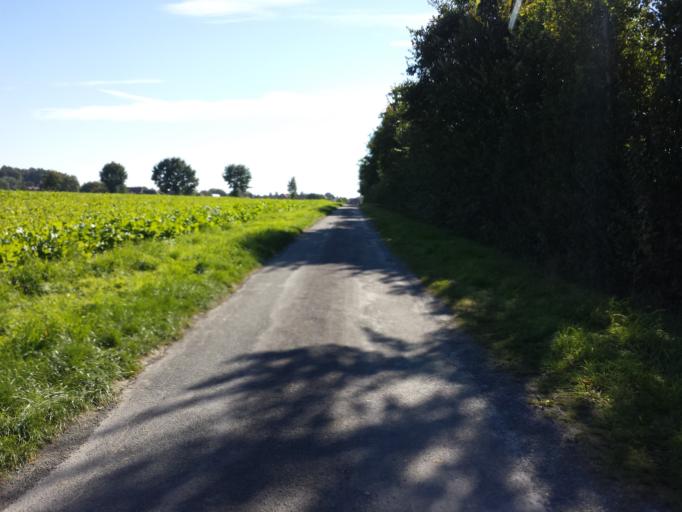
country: DE
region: North Rhine-Westphalia
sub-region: Regierungsbezirk Detmold
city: Langenberg
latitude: 51.7946
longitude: 8.3230
